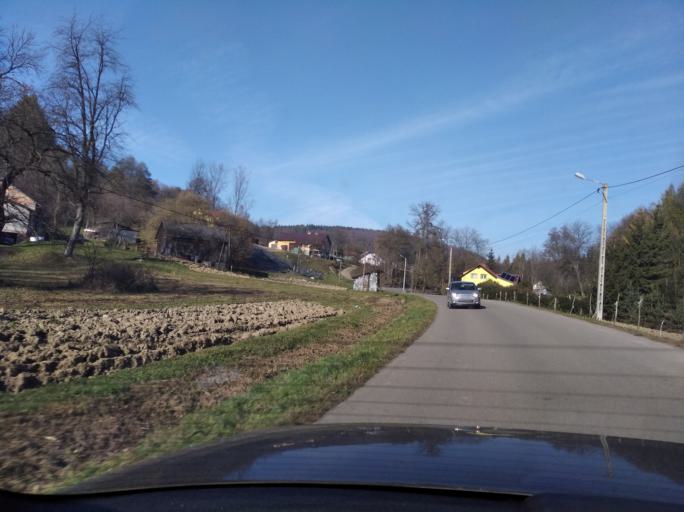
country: PL
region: Subcarpathian Voivodeship
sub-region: Powiat strzyzowski
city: Frysztak
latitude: 49.8905
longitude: 21.6019
